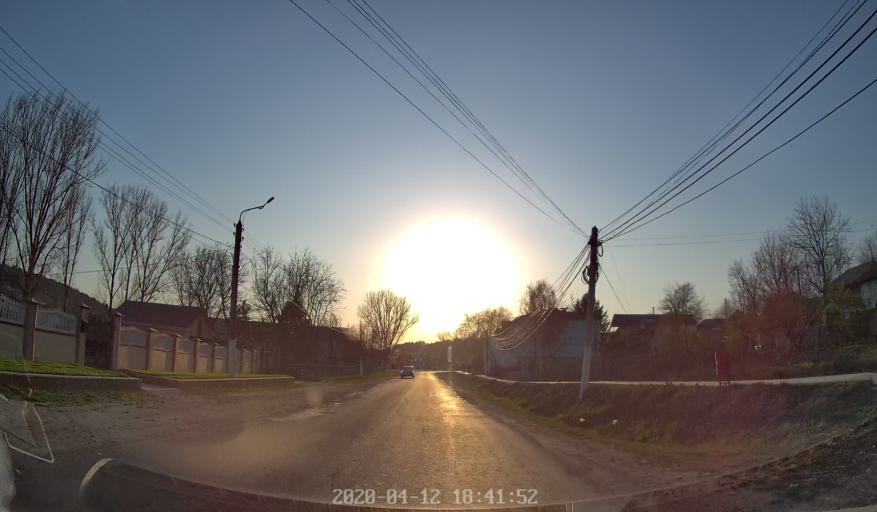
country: MD
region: Chisinau
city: Ciorescu
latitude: 47.1357
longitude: 28.9450
